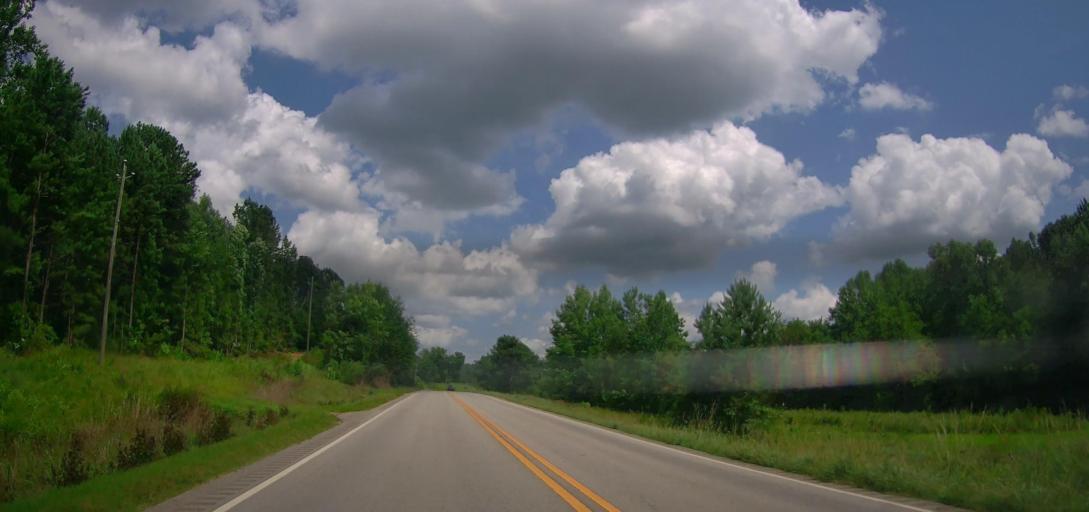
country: US
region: Alabama
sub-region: Cleburne County
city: Heflin
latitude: 33.5742
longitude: -85.4521
